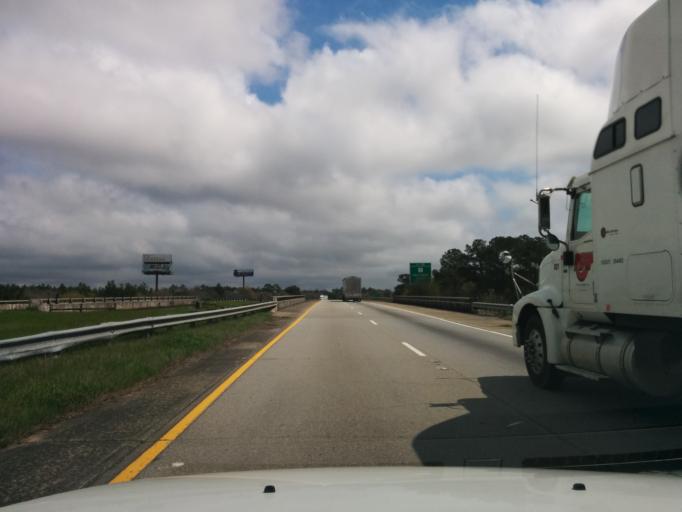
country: US
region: Georgia
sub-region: Emanuel County
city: Swainsboro
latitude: 32.4082
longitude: -82.3271
